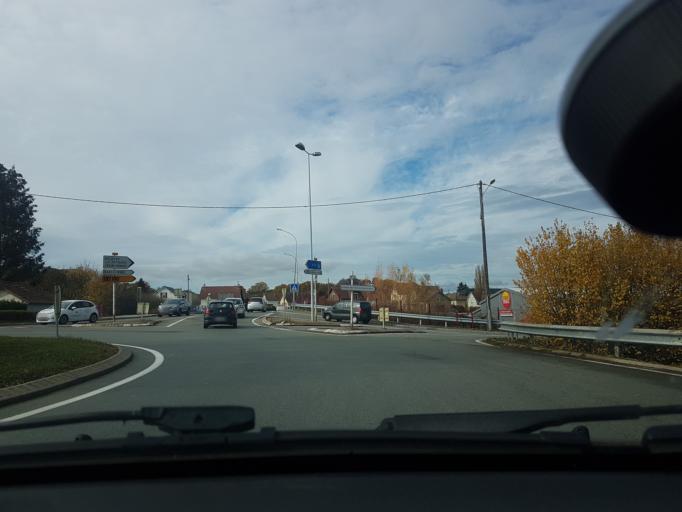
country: FR
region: Franche-Comte
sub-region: Territoire de Belfort
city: Danjoutin
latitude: 47.6184
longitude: 6.8523
